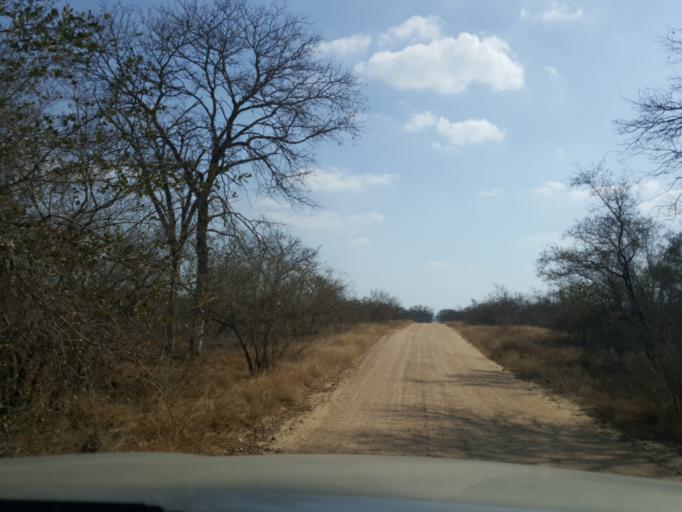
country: ZA
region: Mpumalanga
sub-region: Ehlanzeni District
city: Komatipoort
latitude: -25.2725
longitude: 31.8091
